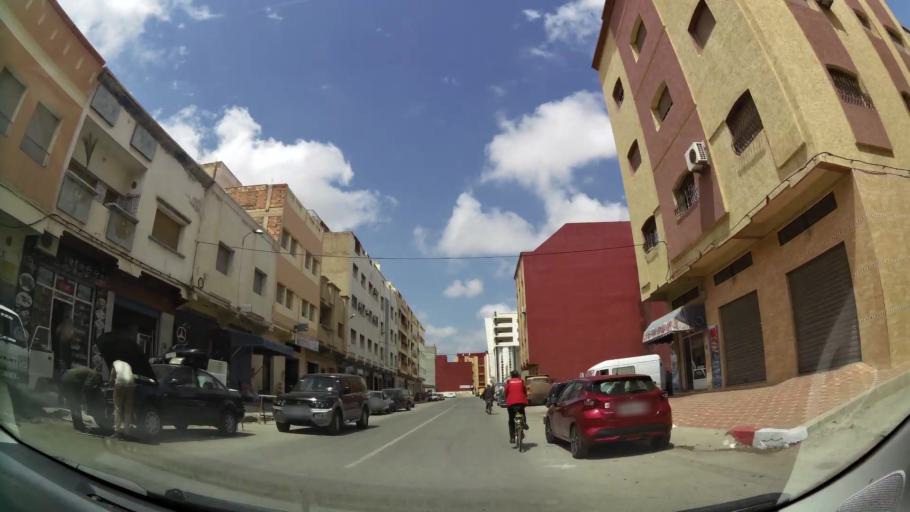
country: MA
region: Oriental
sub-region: Nador
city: Nador
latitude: 35.1659
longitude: -2.9271
